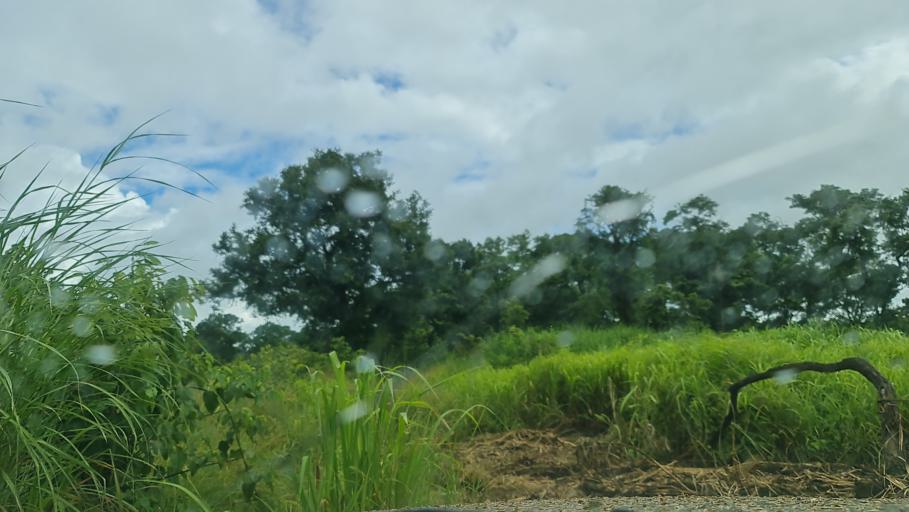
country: MW
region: Southern Region
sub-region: Nsanje District
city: Nsanje
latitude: -17.4474
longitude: 35.8419
